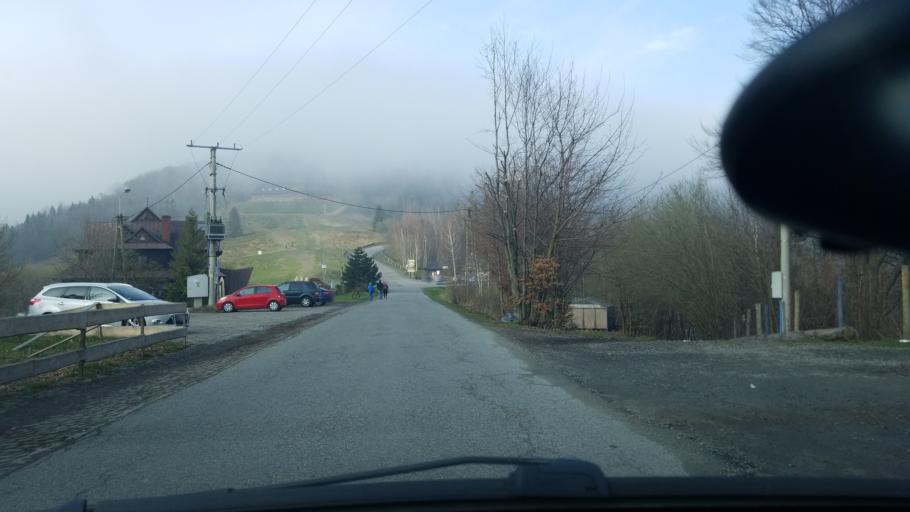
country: PL
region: Silesian Voivodeship
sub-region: Powiat cieszynski
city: Ustron
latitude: 49.7189
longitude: 18.8516
